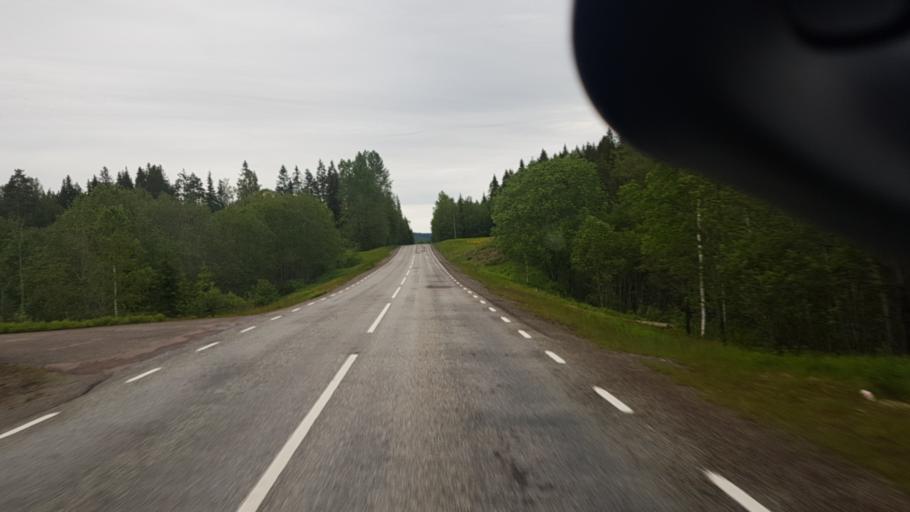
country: SE
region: Vaermland
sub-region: Arjangs Kommun
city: Arjaeng
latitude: 59.5620
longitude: 12.1215
